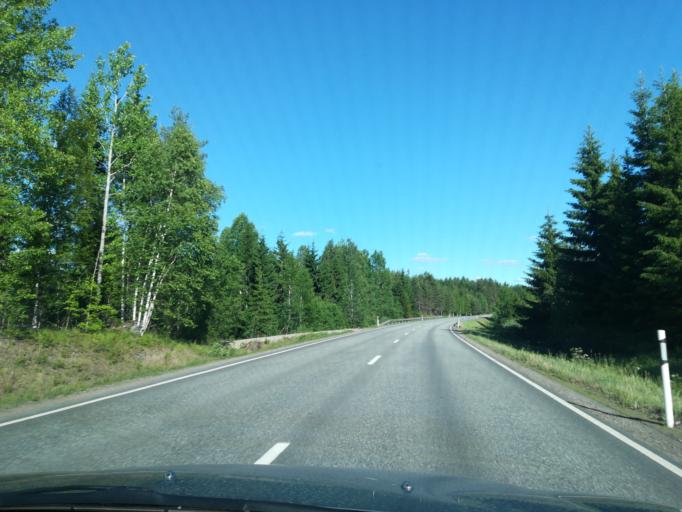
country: FI
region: South Karelia
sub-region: Imatra
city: Ruokolahti
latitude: 61.3496
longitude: 28.7559
